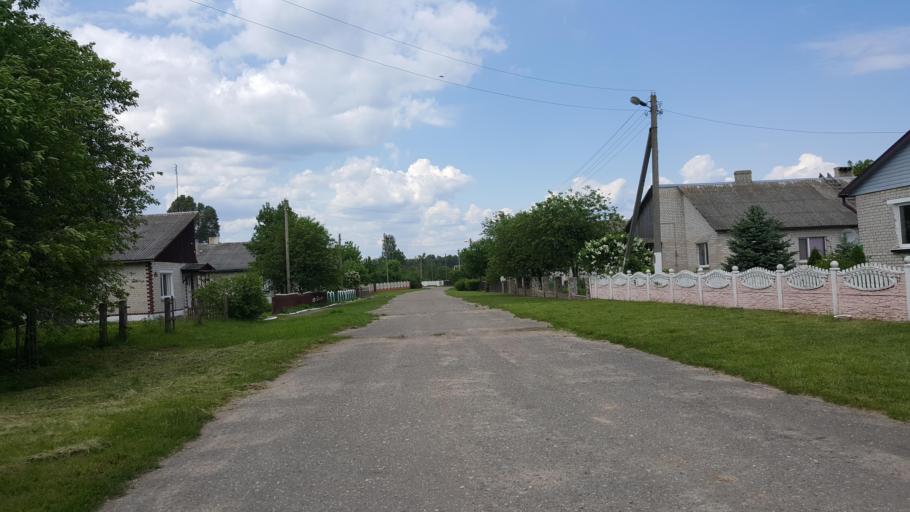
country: PL
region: Podlasie
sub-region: Powiat hajnowski
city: Bialowieza
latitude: 52.6701
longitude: 24.0884
